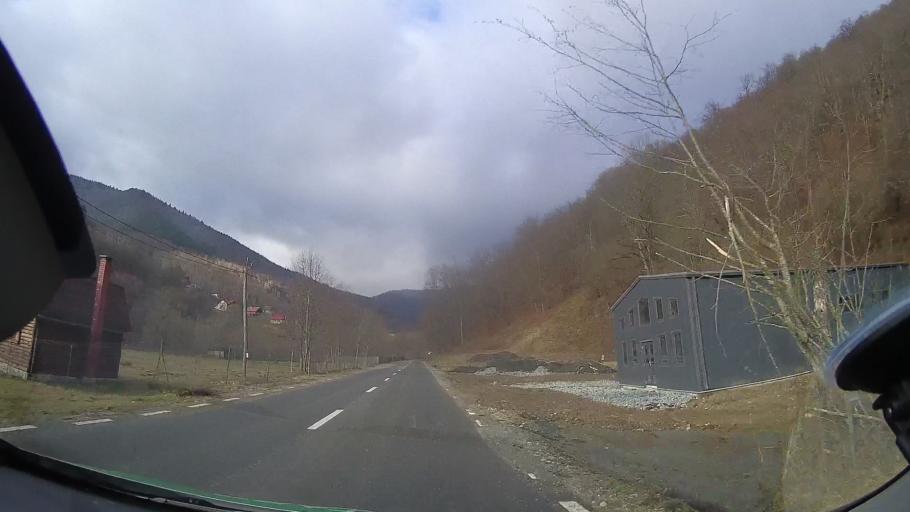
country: RO
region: Cluj
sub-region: Comuna Valea Ierii
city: Valea Ierii
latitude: 46.6393
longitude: 23.3616
